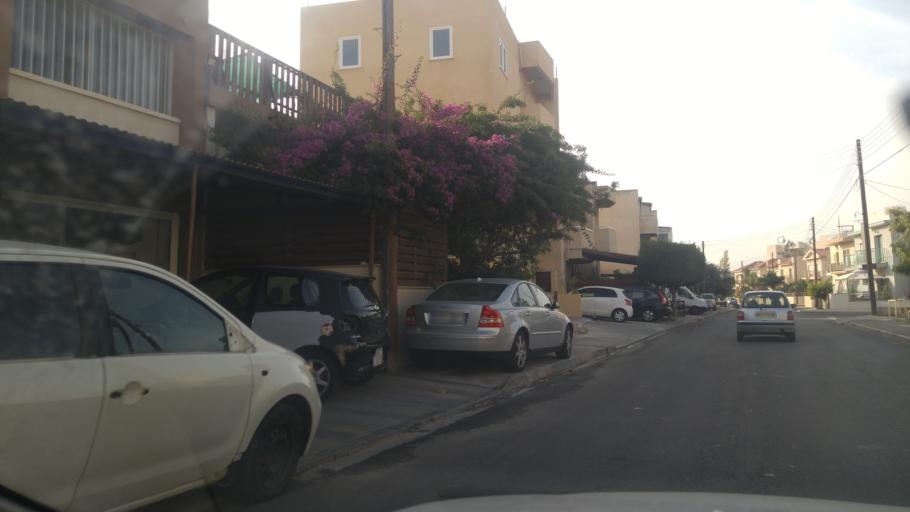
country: CY
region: Limassol
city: Limassol
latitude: 34.6621
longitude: 33.0032
